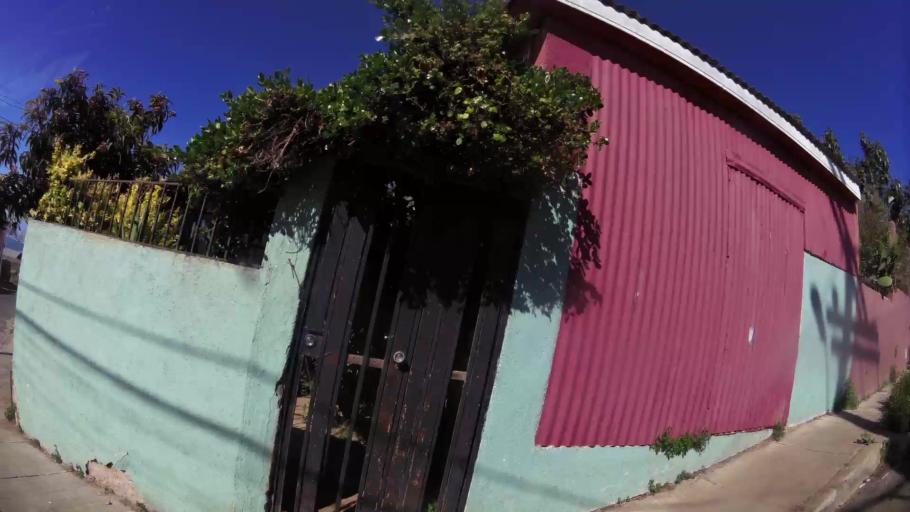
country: CL
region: Valparaiso
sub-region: Provincia de Valparaiso
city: Vina del Mar
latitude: -33.0454
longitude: -71.5602
